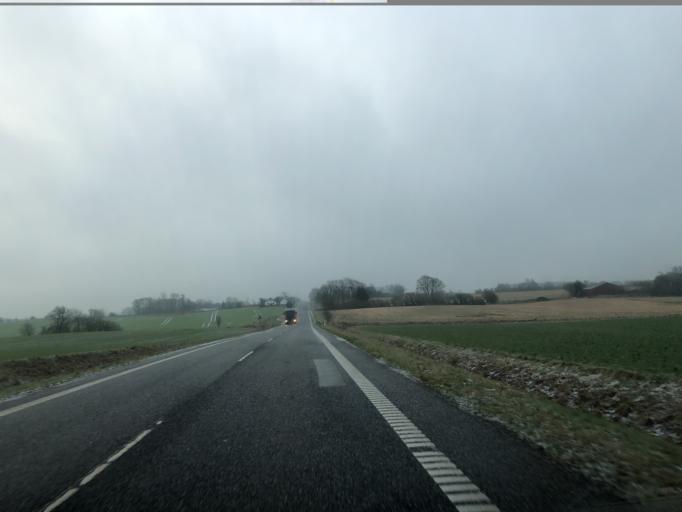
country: DK
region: South Denmark
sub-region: Vejle Kommune
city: Jelling
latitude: 55.7768
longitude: 9.3970
